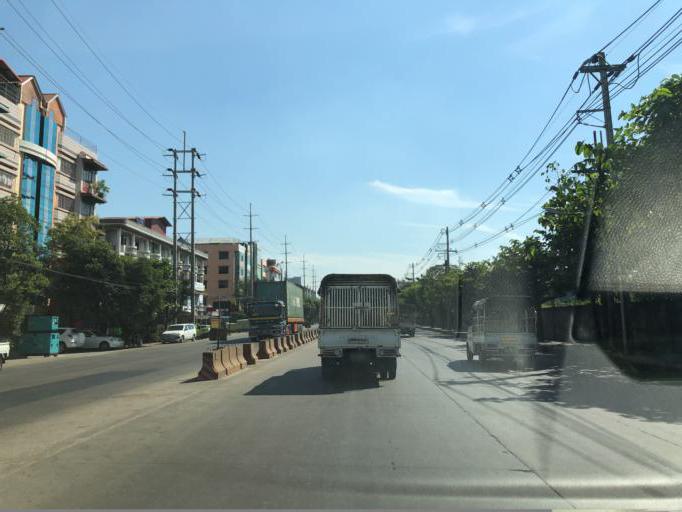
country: MM
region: Yangon
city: Yangon
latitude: 16.8288
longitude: 96.1221
